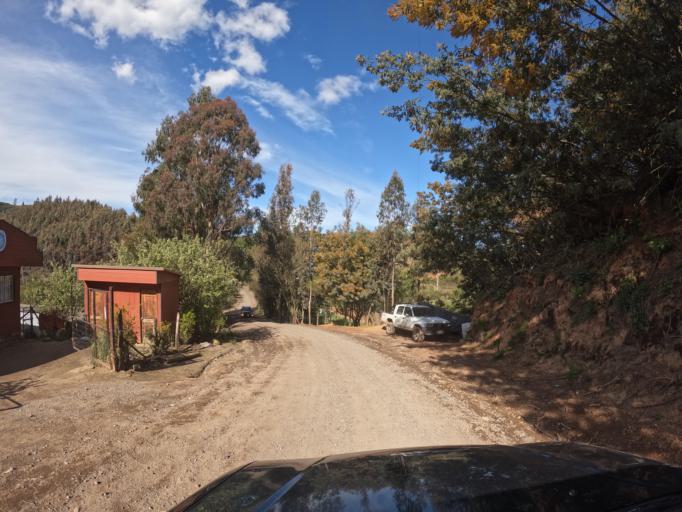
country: CL
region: Biobio
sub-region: Provincia de Concepcion
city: Chiguayante
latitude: -37.0675
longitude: -72.8517
